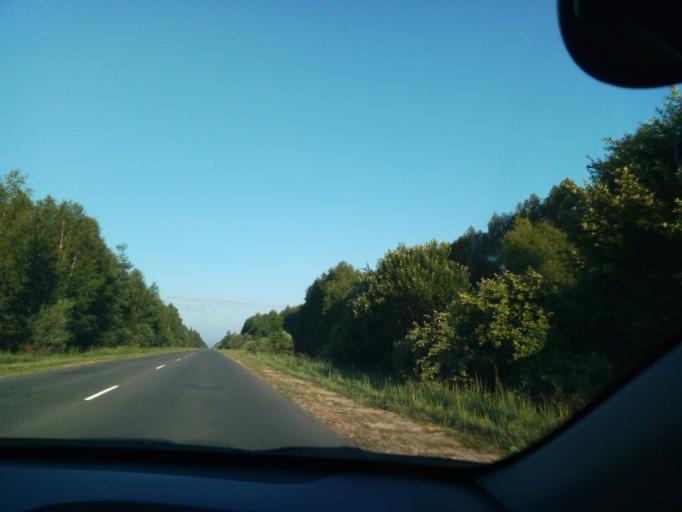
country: RU
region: Nizjnij Novgorod
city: Satis
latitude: 54.8993
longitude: 43.1287
